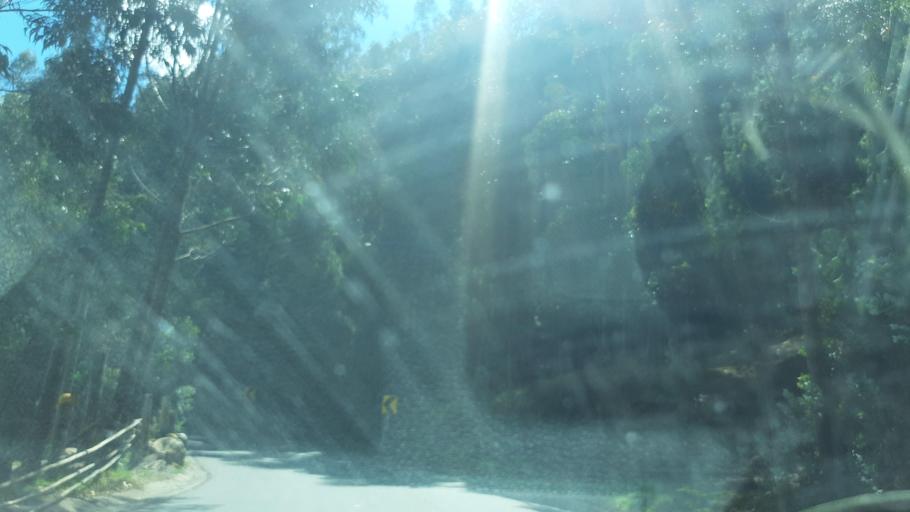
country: CO
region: Boyaca
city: Samaca
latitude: 5.4833
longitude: -73.4786
